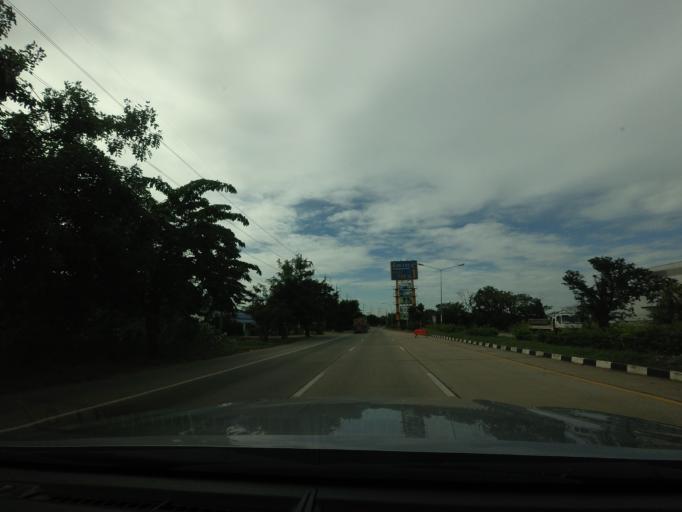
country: TH
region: Suphan Buri
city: Doem Bang Nang Buat
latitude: 14.9056
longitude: 100.0862
